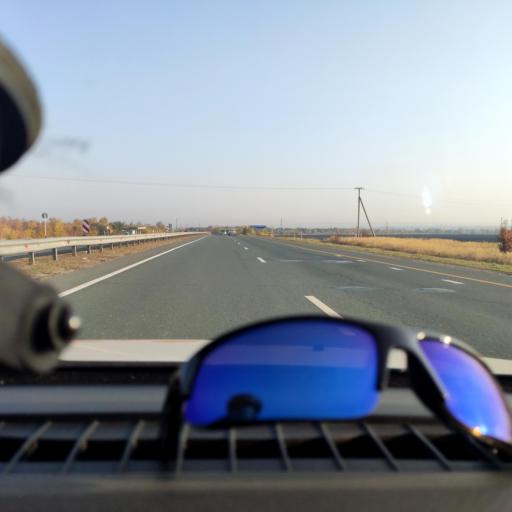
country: RU
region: Samara
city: Novokuybyshevsk
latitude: 53.0130
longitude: 49.9806
